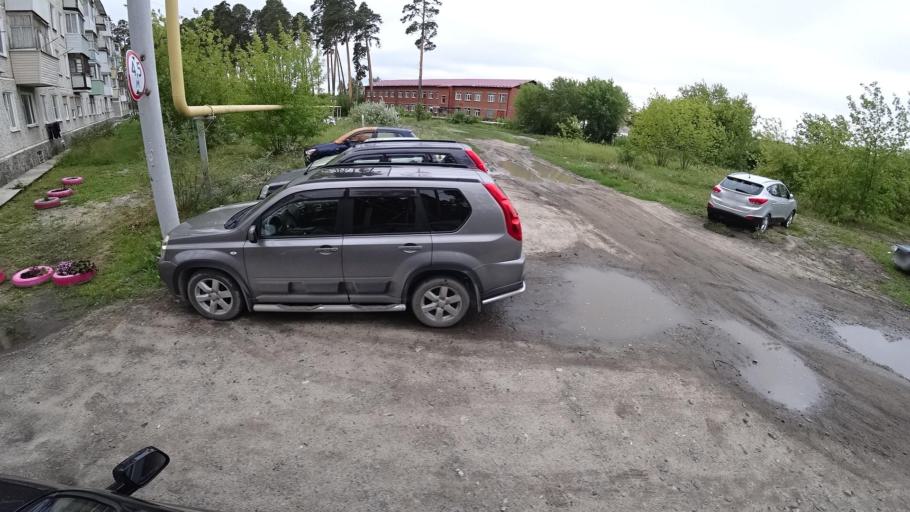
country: RU
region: Sverdlovsk
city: Kamyshlov
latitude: 56.8405
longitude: 62.7431
